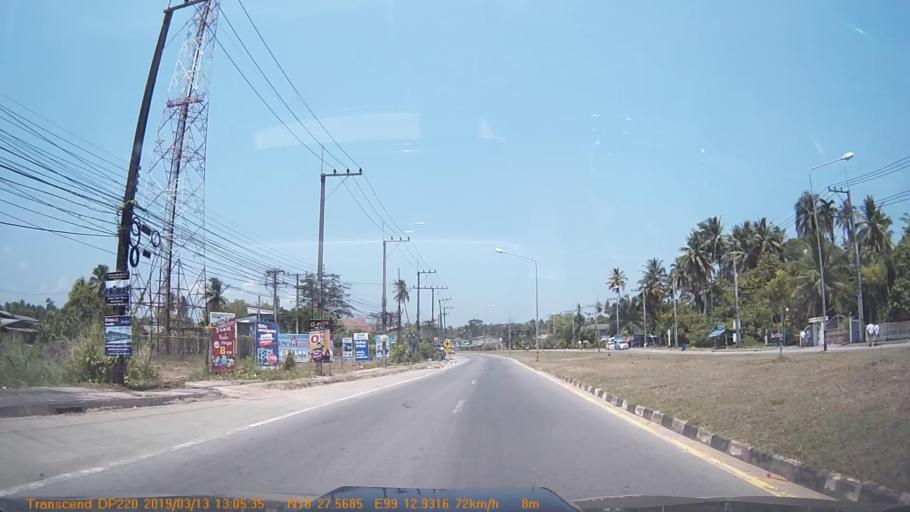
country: TH
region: Chumphon
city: Chumphon
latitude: 10.4600
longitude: 99.2157
